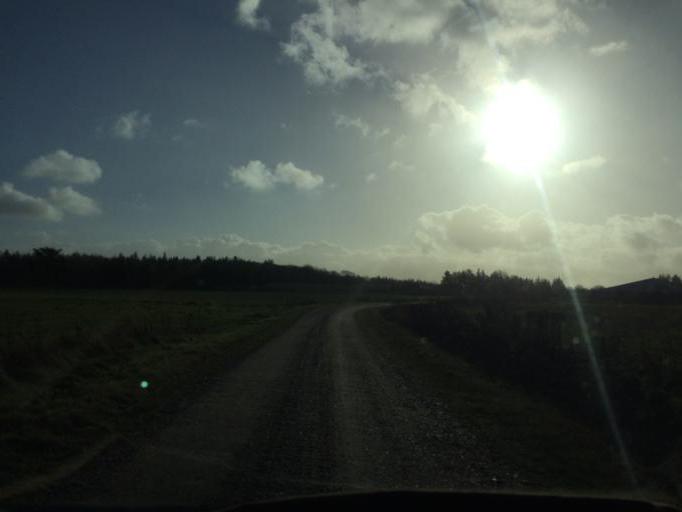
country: DK
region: Central Jutland
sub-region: Holstebro Kommune
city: Ulfborg
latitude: 56.2392
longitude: 8.4477
